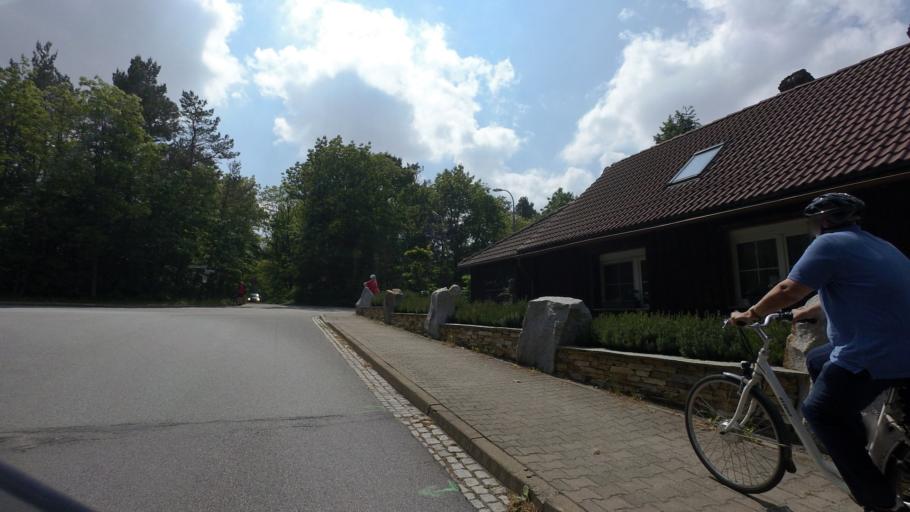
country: DE
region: Saxony
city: Weisswasser
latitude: 51.5001
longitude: 14.6148
